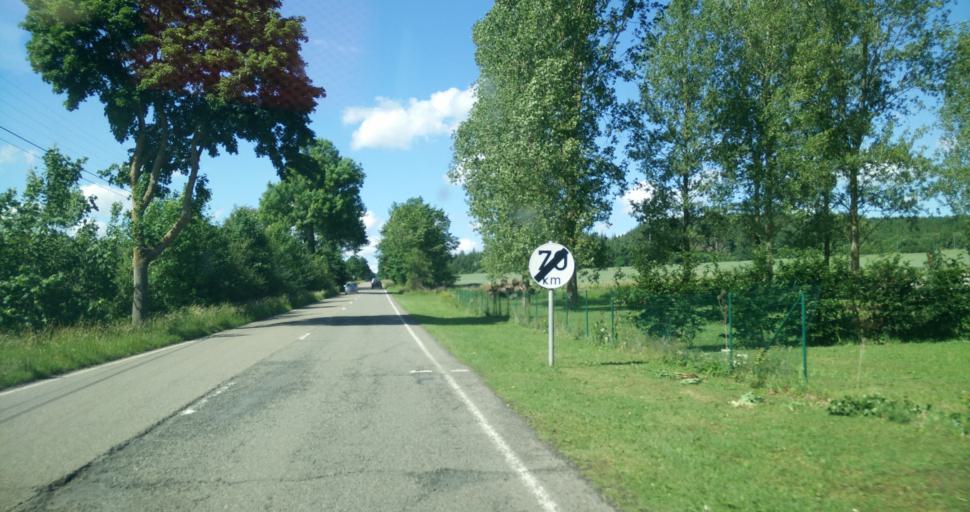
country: BE
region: Wallonia
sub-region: Province du Luxembourg
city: Marche-en-Famenne
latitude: 50.1923
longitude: 5.3659
